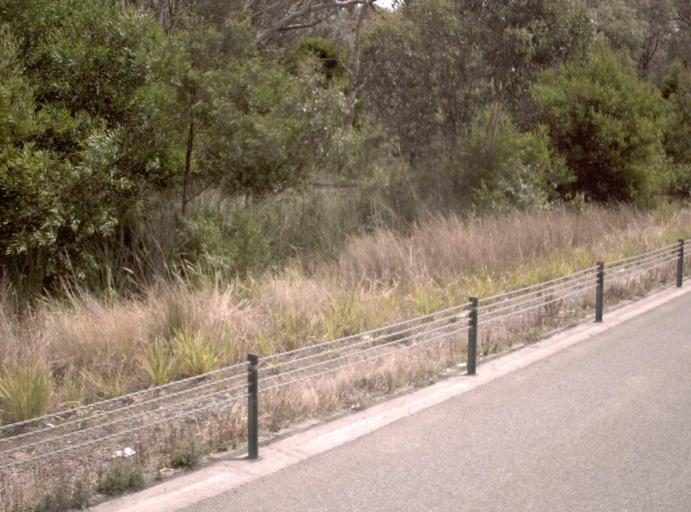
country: AU
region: Victoria
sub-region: Casey
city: Cranbourne South
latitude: -38.1656
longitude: 145.2222
